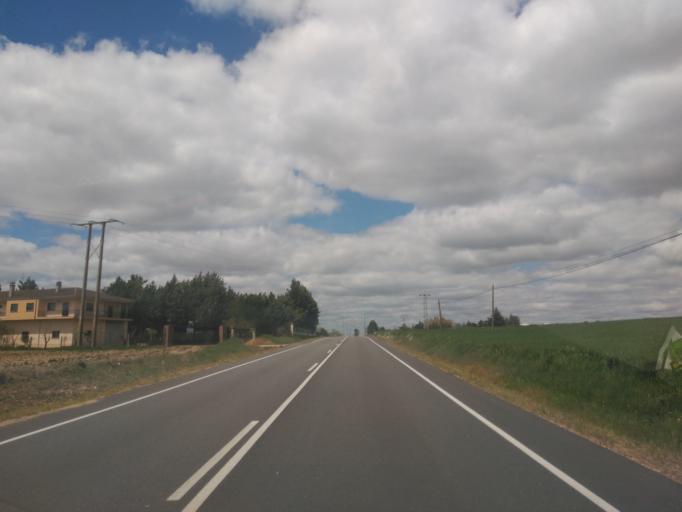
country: ES
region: Castille and Leon
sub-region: Provincia de Salamanca
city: Villamayor
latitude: 41.0061
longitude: -5.7037
